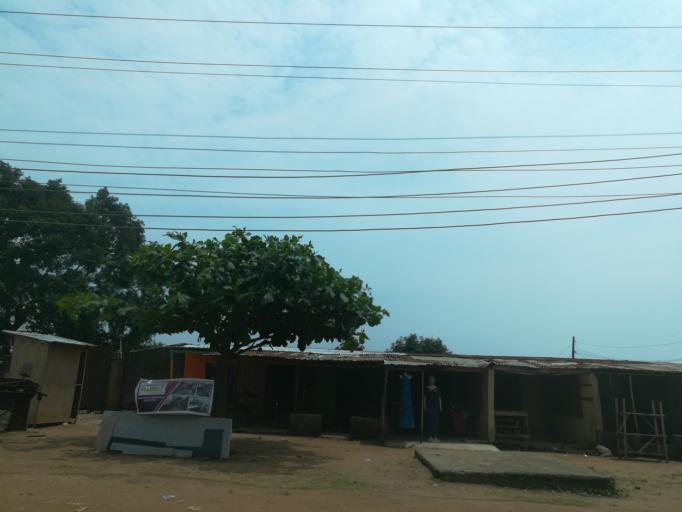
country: NG
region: Lagos
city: Ikorodu
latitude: 6.6027
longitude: 3.6143
